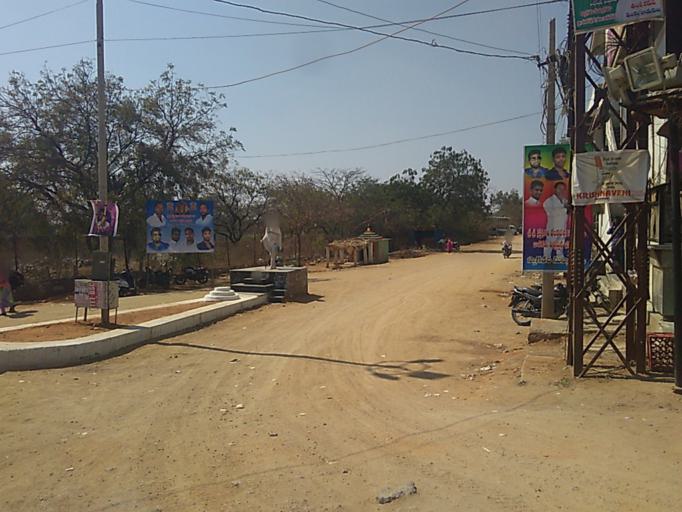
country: IN
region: Telangana
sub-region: Rangareddi
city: Secunderabad
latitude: 17.6264
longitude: 78.5698
